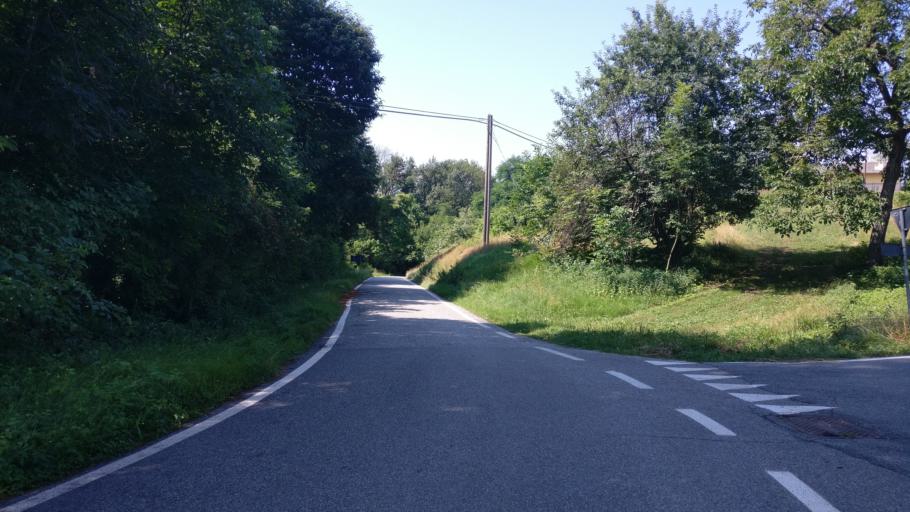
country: IT
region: Piedmont
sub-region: Provincia di Vercelli
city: San Maurizio
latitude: 45.6092
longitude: 8.2993
